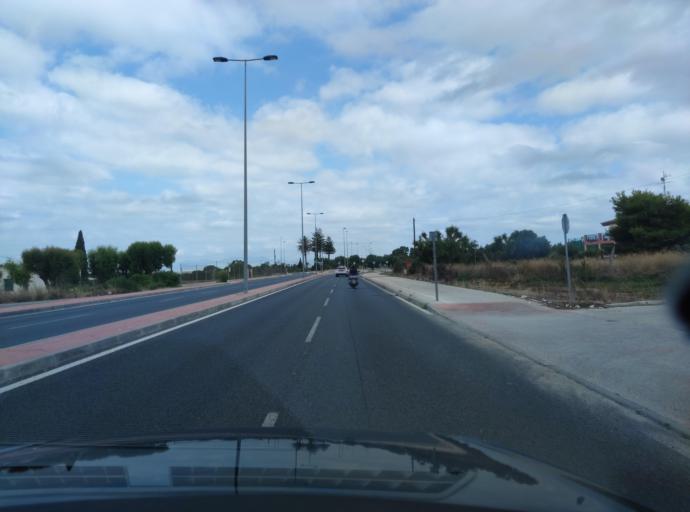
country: ES
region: Valencia
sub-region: Provincia de Alicante
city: Santa Pola
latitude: 38.2044
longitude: -0.5782
